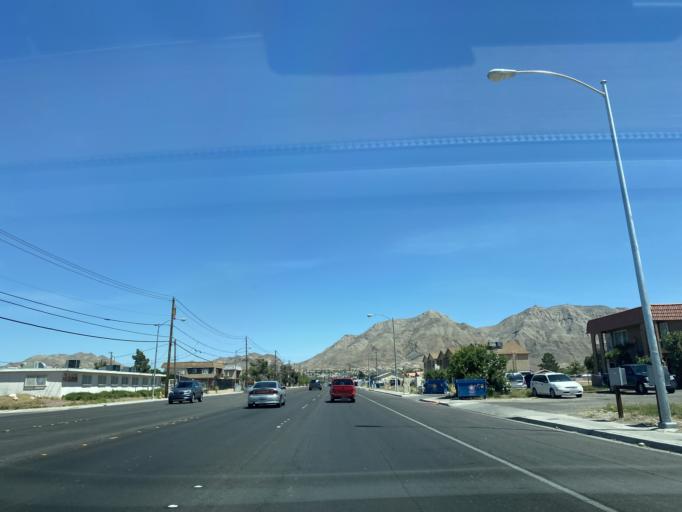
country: US
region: Nevada
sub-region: Clark County
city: Sunrise Manor
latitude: 36.1962
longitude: -115.0511
